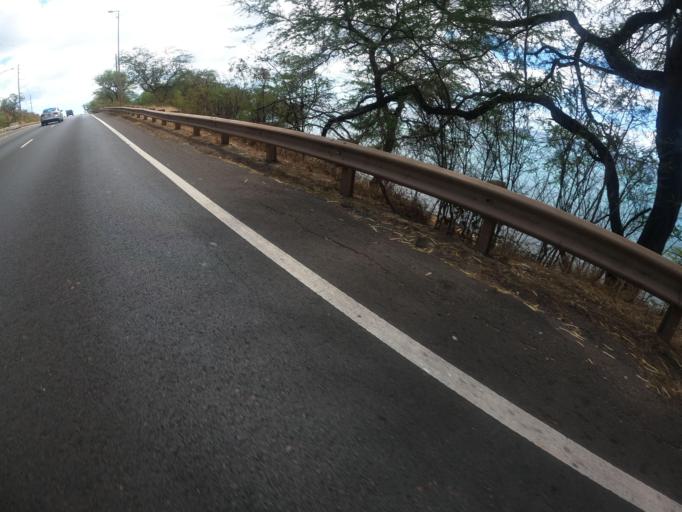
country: US
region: Hawaii
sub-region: Honolulu County
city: Nanakuli
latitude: 21.3687
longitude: -158.1357
